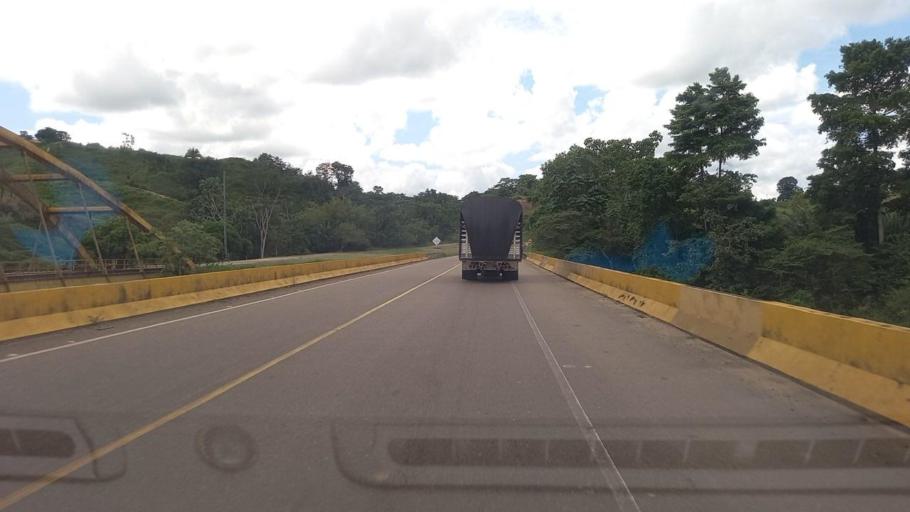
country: CO
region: Antioquia
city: Yondo
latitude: 6.8561
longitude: -73.7695
